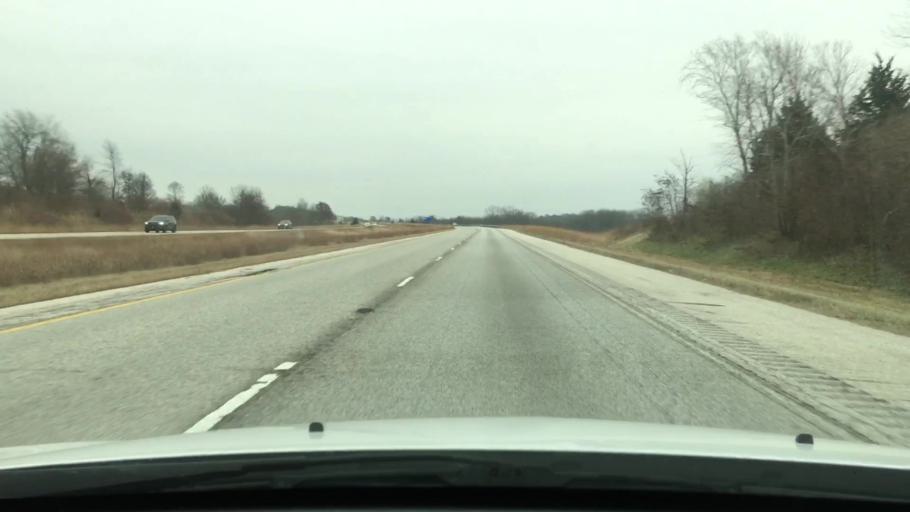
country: US
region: Illinois
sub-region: Morgan County
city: South Jacksonville
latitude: 39.6803
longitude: -90.2719
